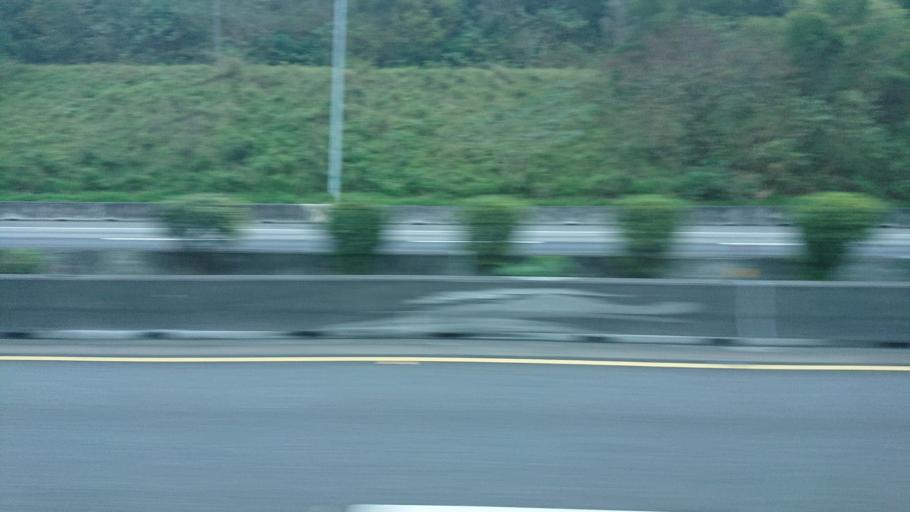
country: TW
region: Taiwan
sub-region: Miaoli
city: Miaoli
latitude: 24.5016
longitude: 120.7897
